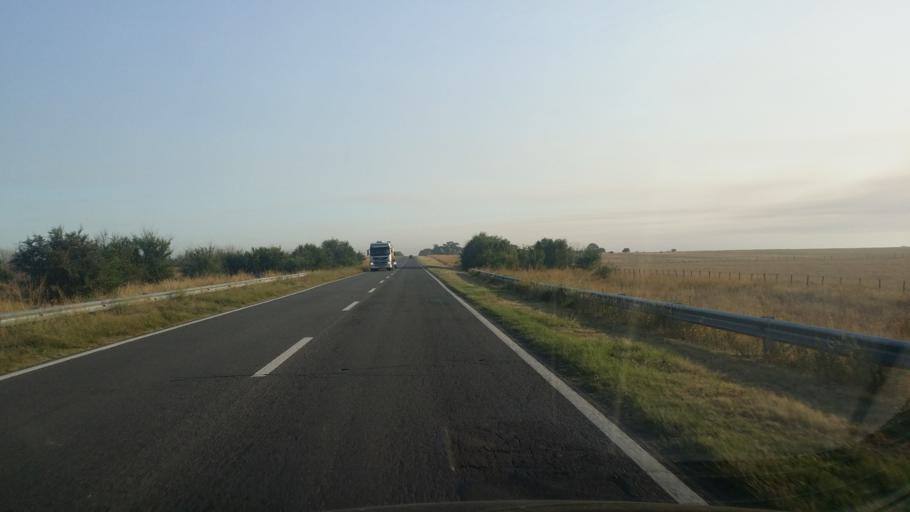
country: AR
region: La Pampa
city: Santa Rosa
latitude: -36.4540
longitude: -64.2801
